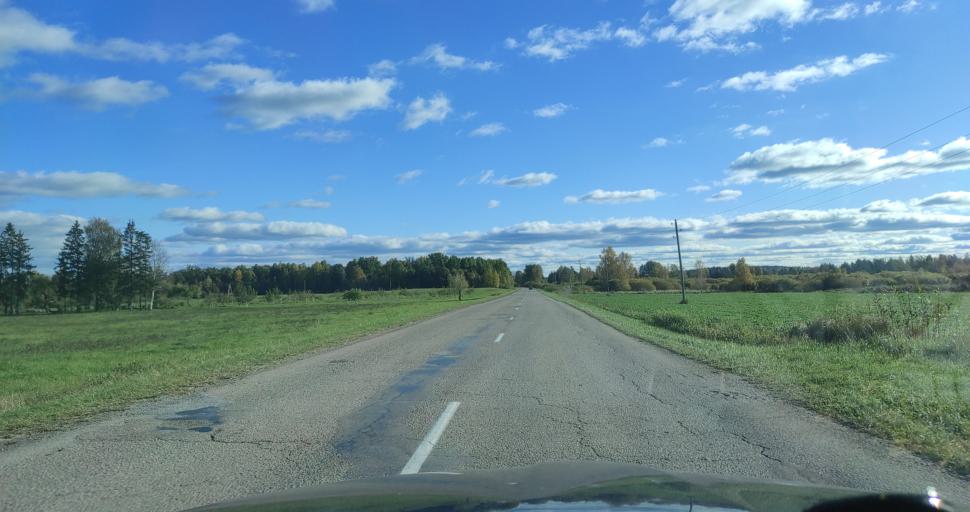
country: LV
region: Aizpute
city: Aizpute
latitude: 56.7958
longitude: 21.5022
